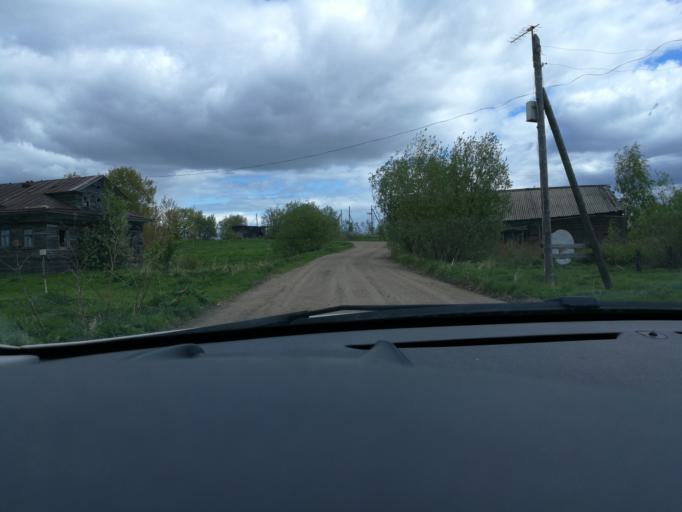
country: RU
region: Arkhangelskaya
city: Lukovetskiy
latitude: 64.2528
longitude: 41.7904
